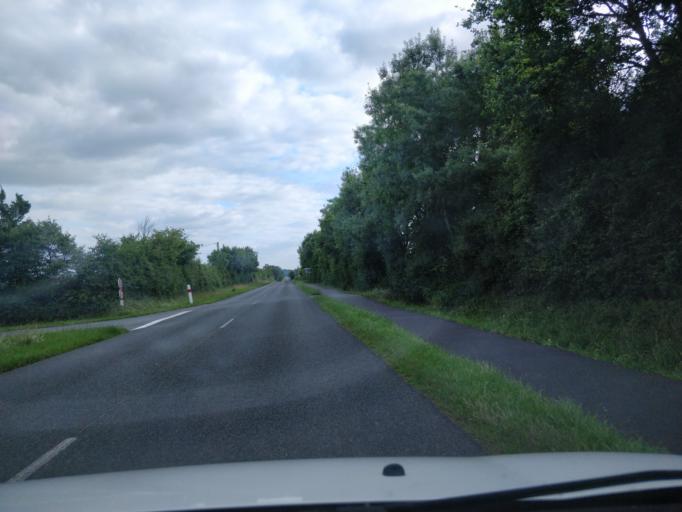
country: FR
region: Pays de la Loire
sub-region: Departement de Maine-et-Loire
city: Feneu
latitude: 47.5617
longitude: -0.5985
